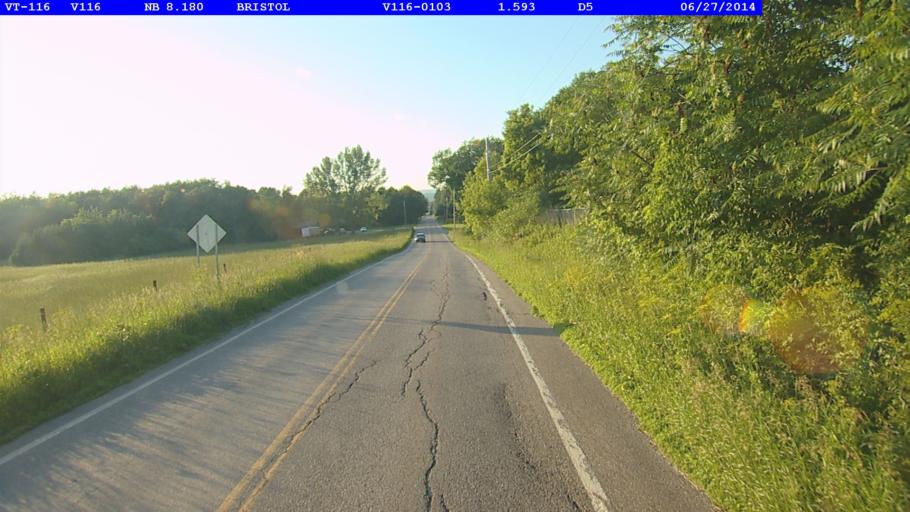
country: US
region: Vermont
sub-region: Addison County
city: Bristol
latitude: 44.0767
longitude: -73.0857
